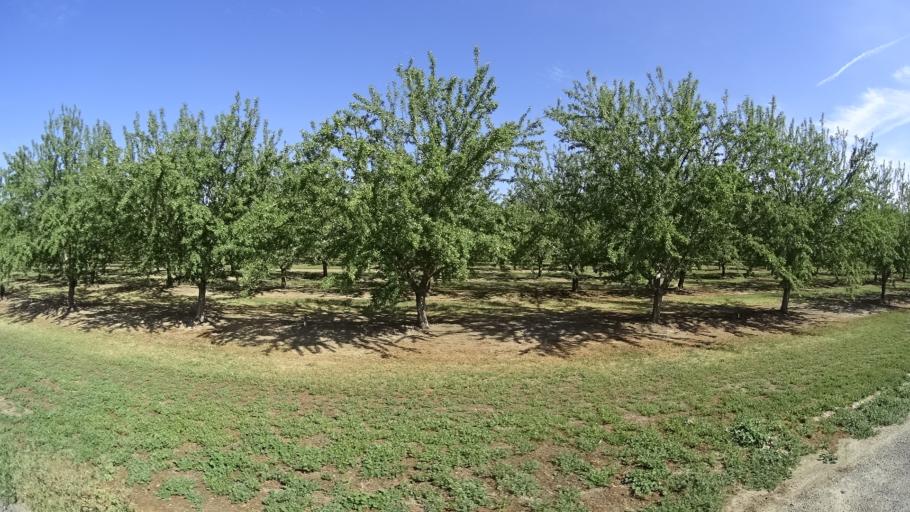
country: US
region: California
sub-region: Glenn County
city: Hamilton City
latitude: 39.6161
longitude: -122.0195
